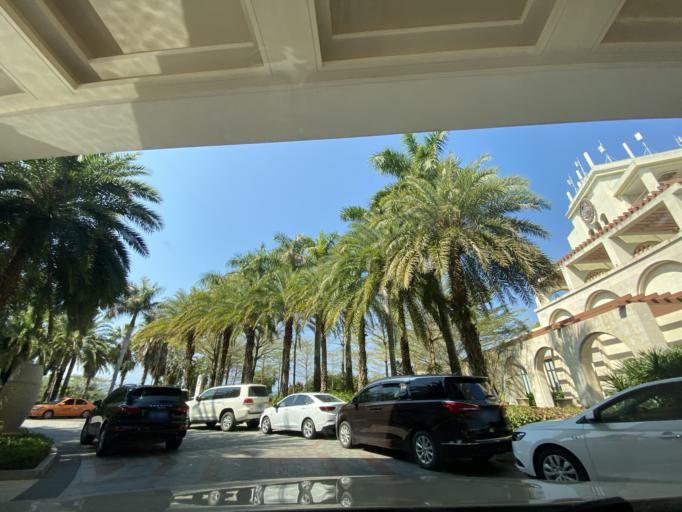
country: CN
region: Hainan
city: Haitangwan
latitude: 18.3482
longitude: 109.7360
